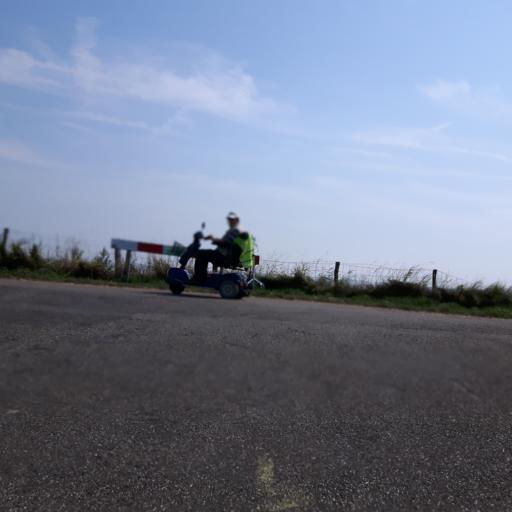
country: NL
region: Zeeland
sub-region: Gemeente Goes
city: Goes
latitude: 51.4512
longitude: 3.9226
